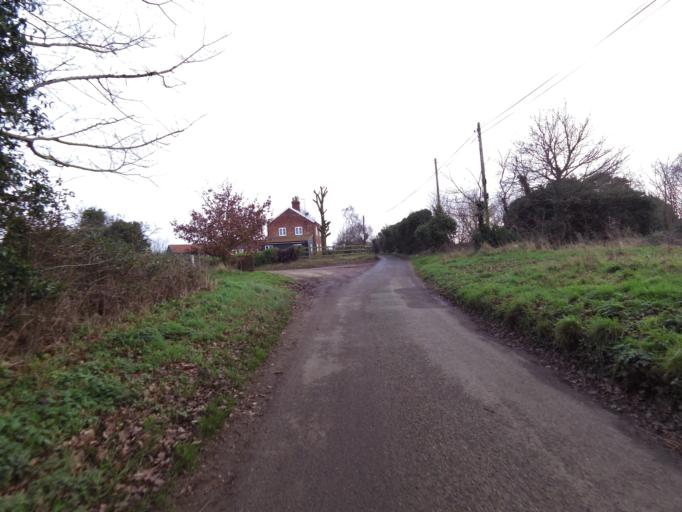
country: GB
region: England
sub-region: Suffolk
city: Woodbridge
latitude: 52.0602
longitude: 1.3147
